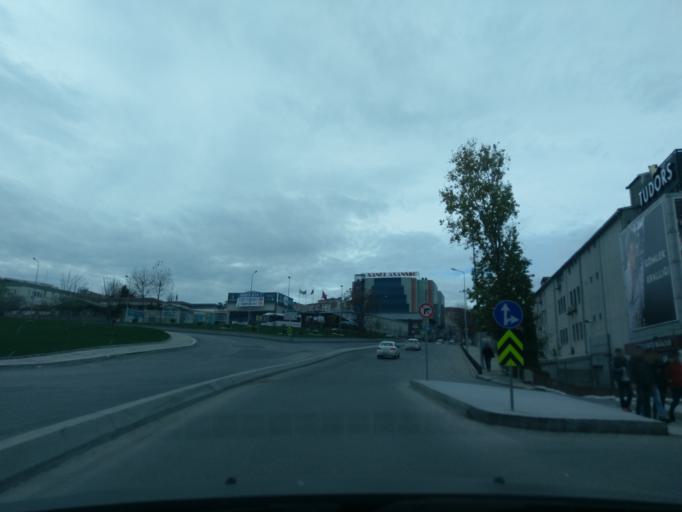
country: TR
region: Istanbul
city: Mahmutbey
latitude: 41.0082
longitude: 28.8087
